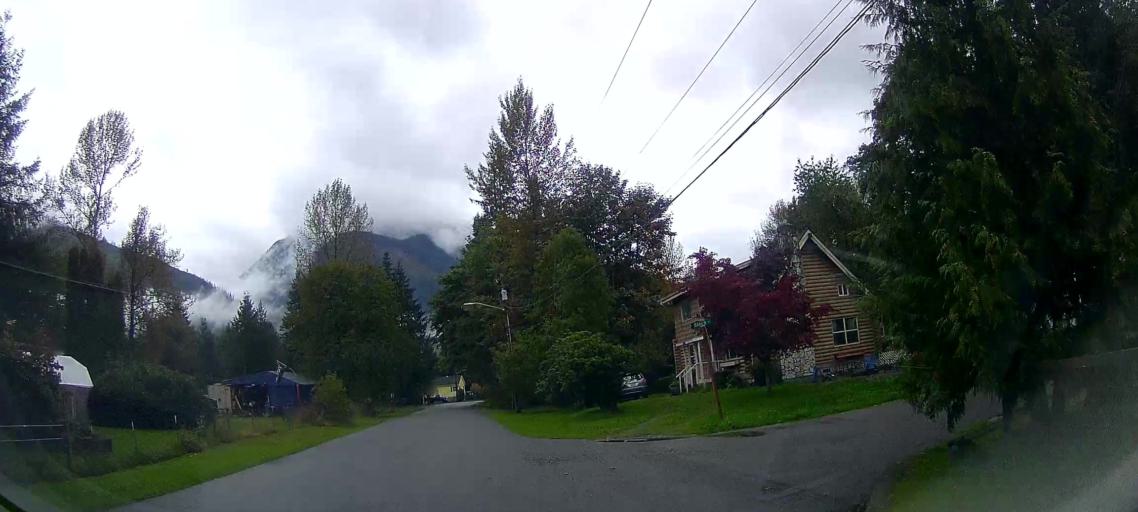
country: US
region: Washington
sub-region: Skagit County
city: Sedro-Woolley
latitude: 48.5246
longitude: -121.9903
